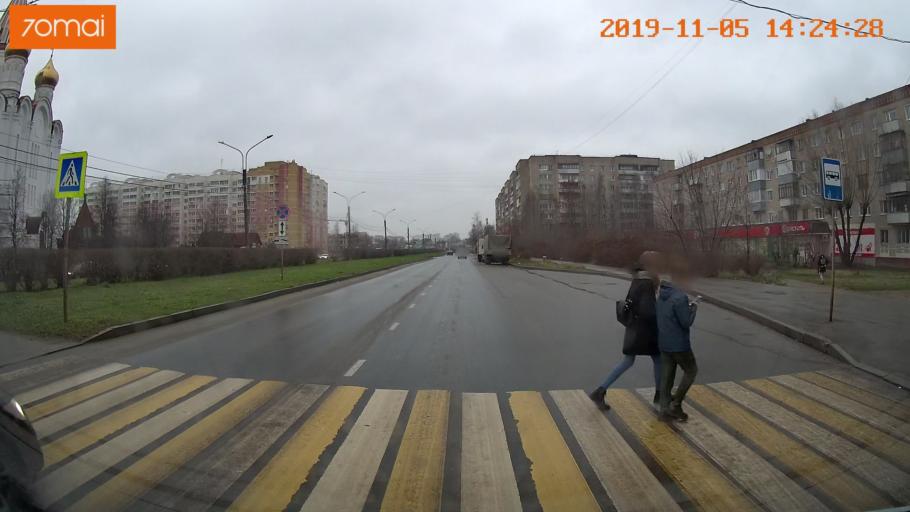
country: RU
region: Ivanovo
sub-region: Gorod Ivanovo
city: Ivanovo
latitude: 56.9686
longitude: 40.9973
